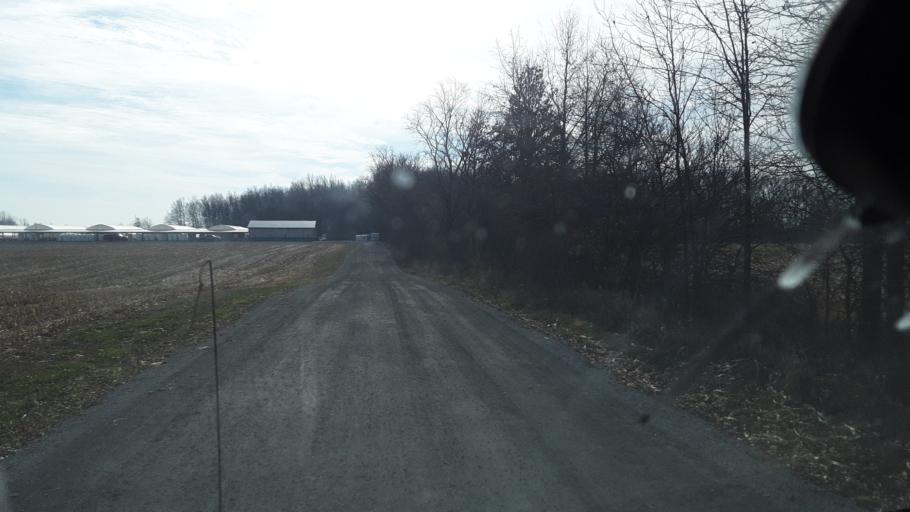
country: US
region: Ohio
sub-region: Defiance County
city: Hicksville
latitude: 41.3513
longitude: -84.7814
